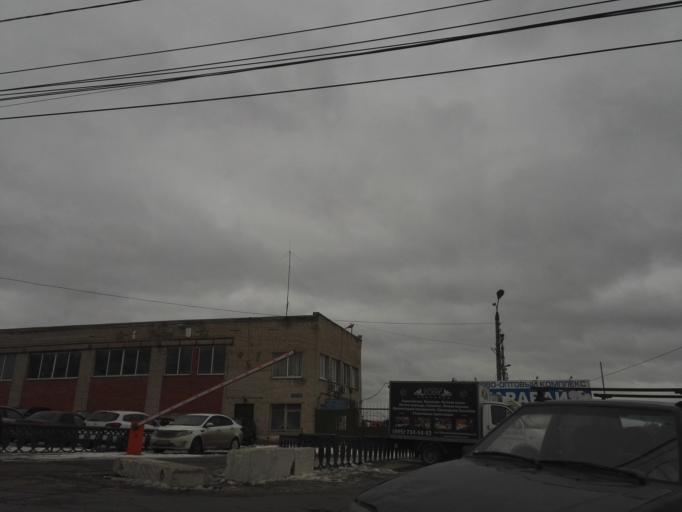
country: RU
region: Tula
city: Tula
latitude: 54.1679
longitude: 37.6413
